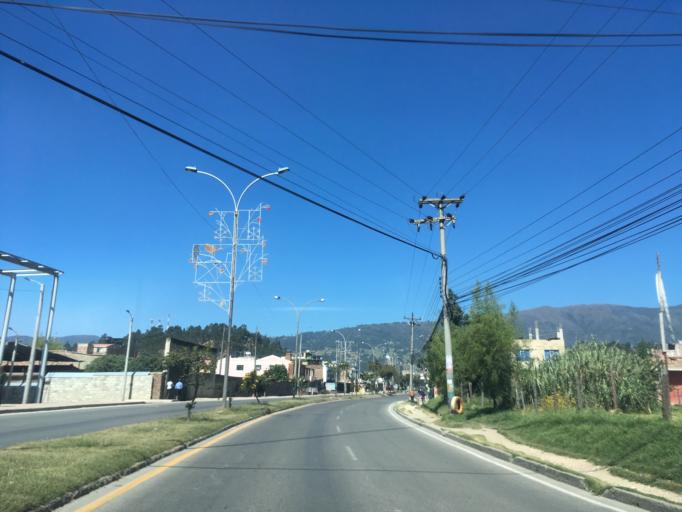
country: CO
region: Boyaca
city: Duitama
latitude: 5.8181
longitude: -73.0227
